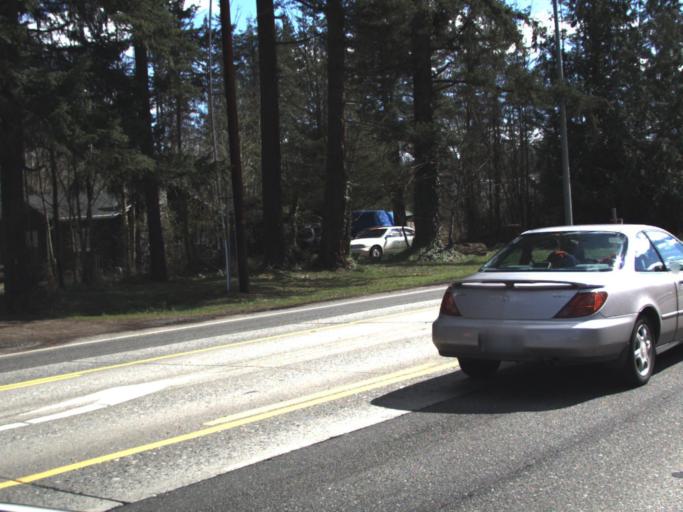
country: US
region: Washington
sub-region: King County
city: Ravensdale
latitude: 47.3564
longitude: -122.0198
